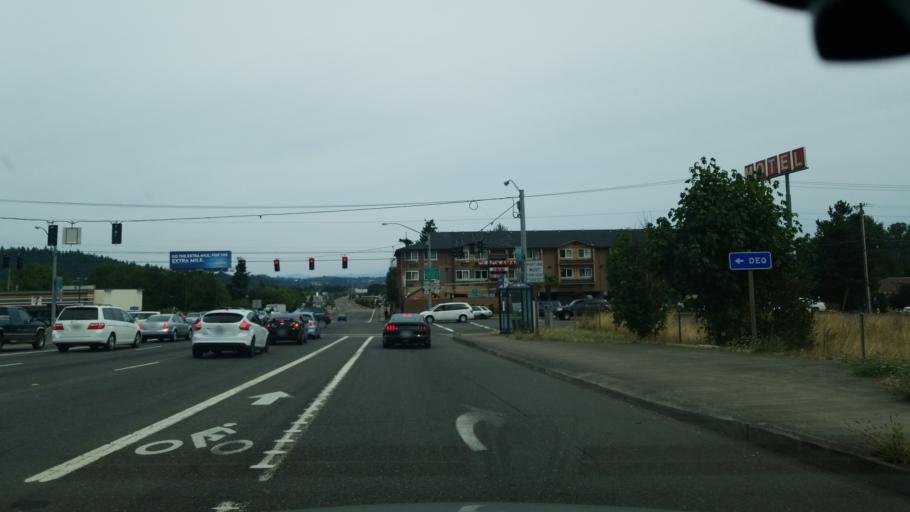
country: US
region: Oregon
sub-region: Clackamas County
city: Clackamas
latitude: 45.4073
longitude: -122.5697
